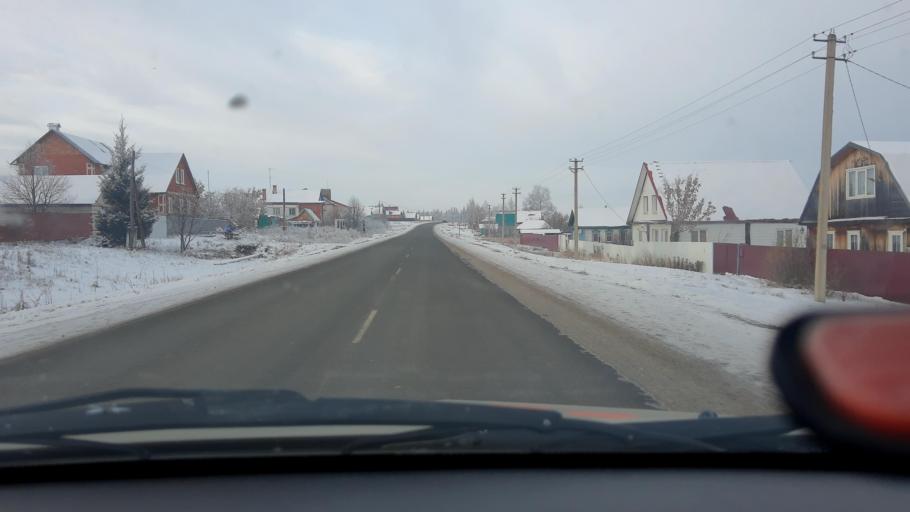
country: RU
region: Bashkortostan
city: Avdon
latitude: 54.3707
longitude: 55.8181
